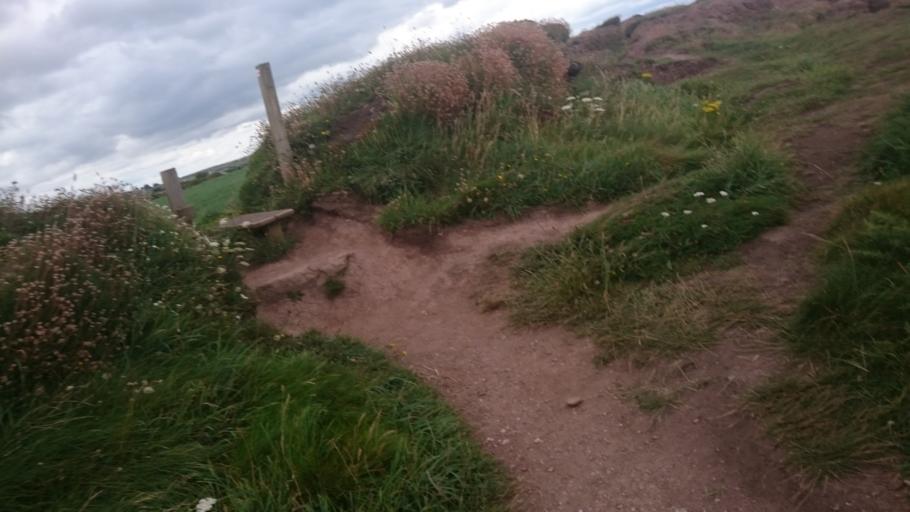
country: IE
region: Munster
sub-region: Waterford
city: Dunmore East
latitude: 52.1419
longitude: -6.9987
